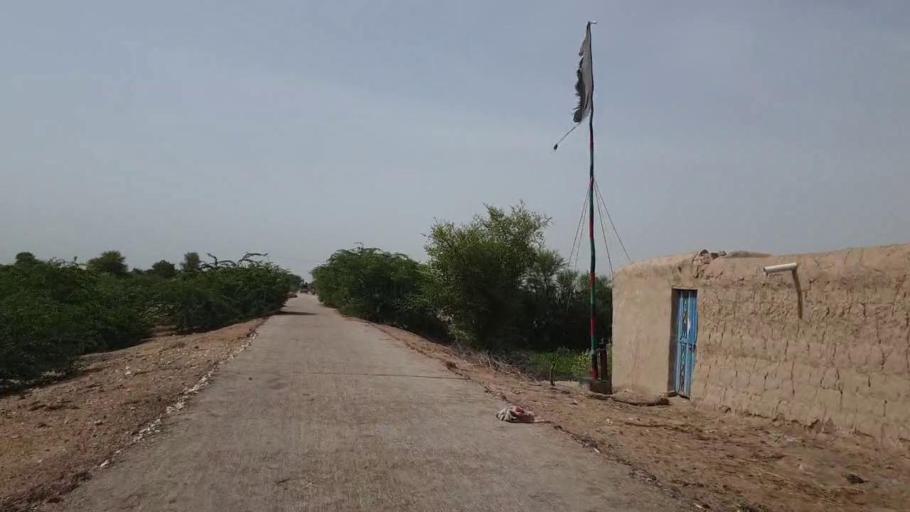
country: PK
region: Sindh
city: Bandhi
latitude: 26.5511
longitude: 68.3840
